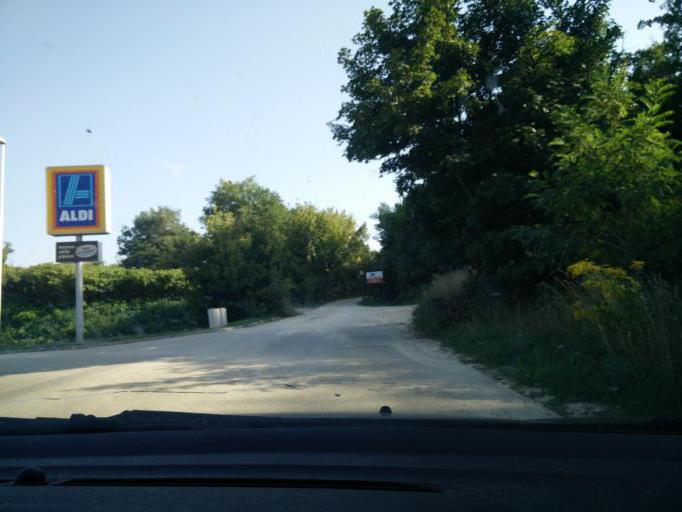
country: HU
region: Pest
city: Piliscsaba
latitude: 47.6279
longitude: 18.8515
